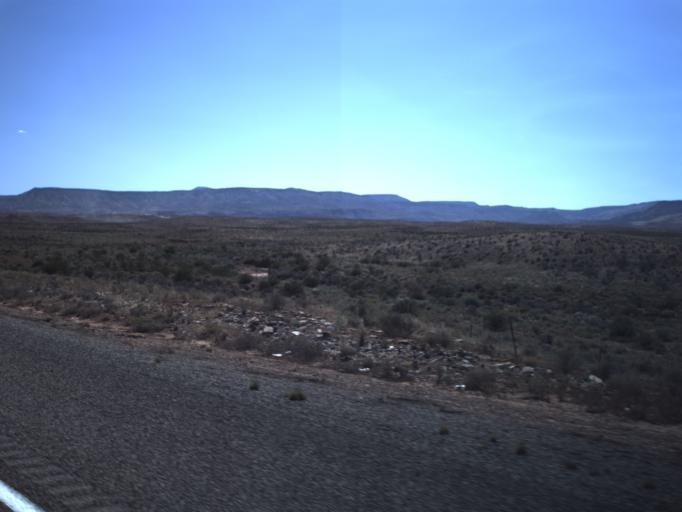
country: US
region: Utah
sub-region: Washington County
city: Saint George
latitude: 37.0043
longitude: -113.5837
